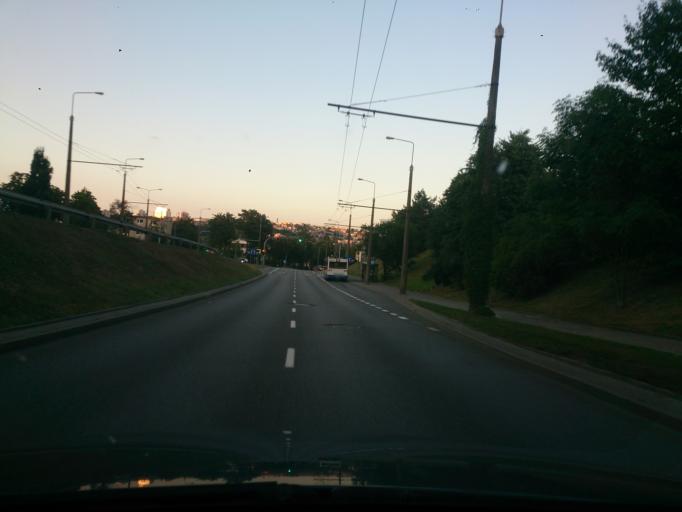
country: PL
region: Pomeranian Voivodeship
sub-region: Gdynia
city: Gdynia
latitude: 54.4806
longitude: 18.5302
